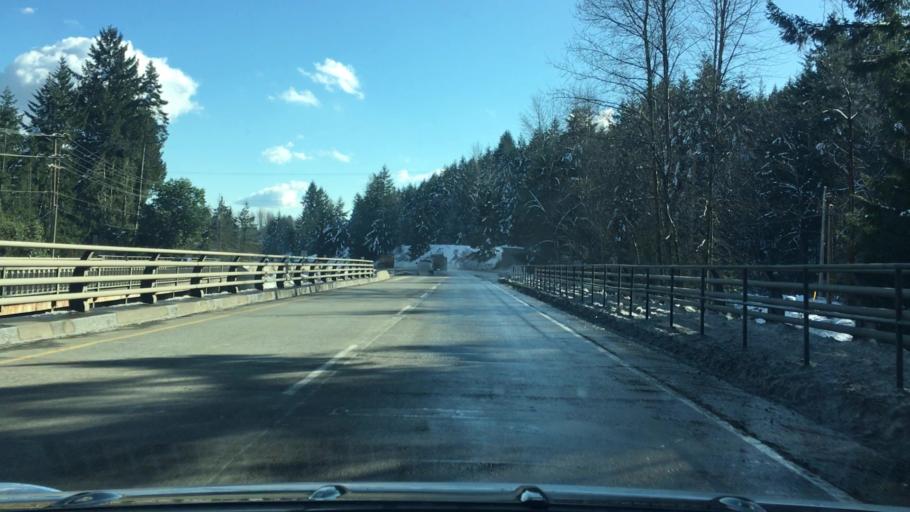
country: CA
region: British Columbia
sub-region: Cowichan Valley Regional District
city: Ladysmith
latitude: 49.0708
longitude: -123.8808
